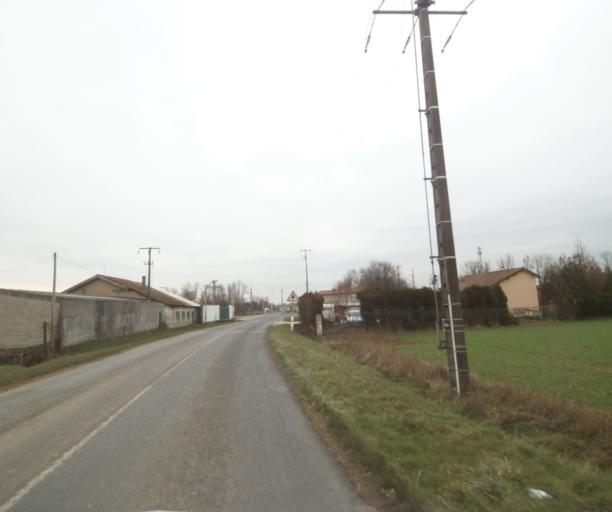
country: FR
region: Champagne-Ardenne
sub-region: Departement de la Haute-Marne
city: Villiers-en-Lieu
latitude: 48.6585
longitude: 4.9091
